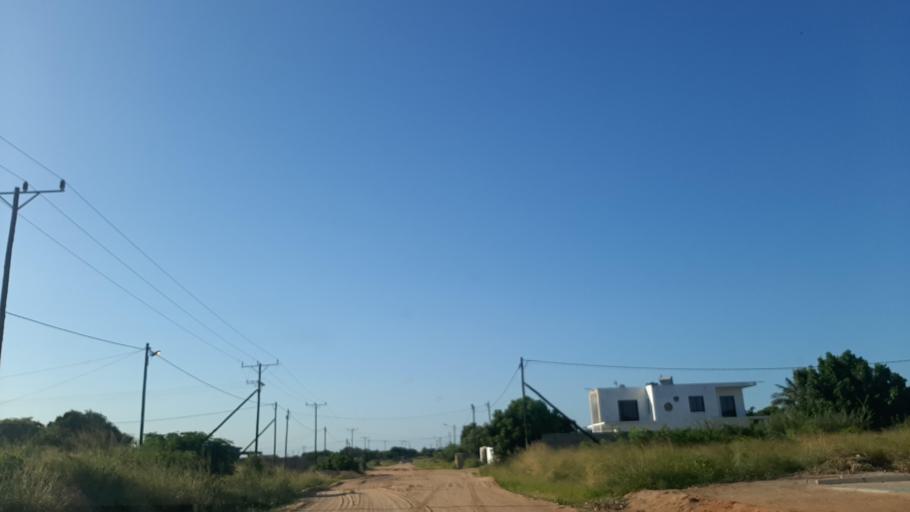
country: MZ
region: Maputo City
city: Maputo
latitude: -25.7681
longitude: 32.5480
